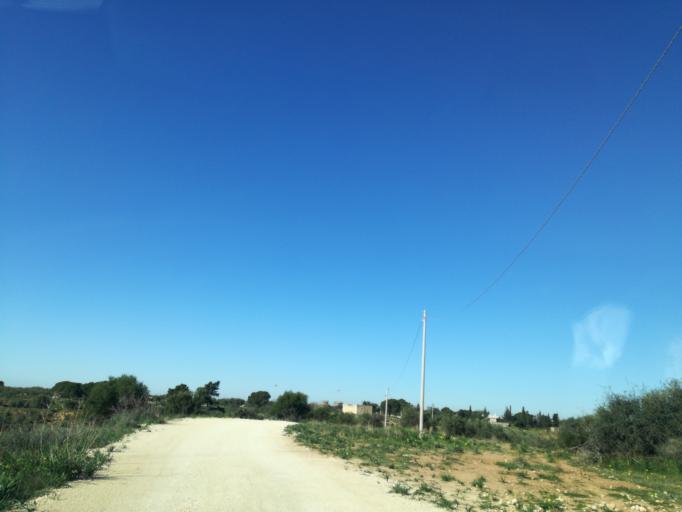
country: IT
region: Sicily
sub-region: Provincia di Caltanissetta
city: Niscemi
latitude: 37.0557
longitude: 14.3619
